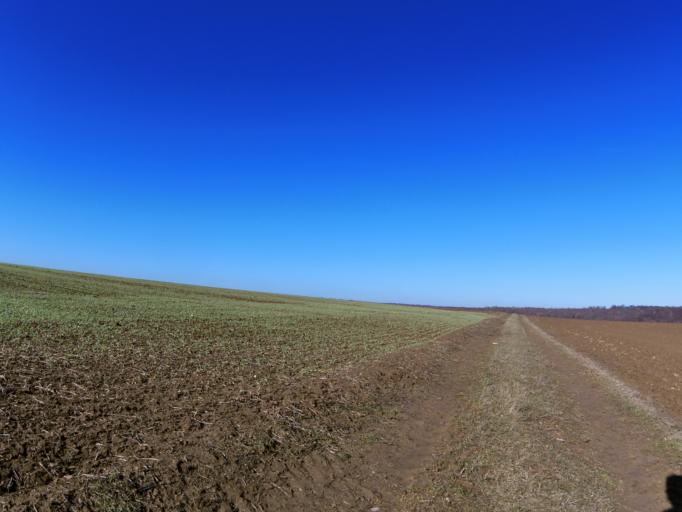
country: DE
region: Bavaria
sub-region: Regierungsbezirk Unterfranken
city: Estenfeld
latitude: 49.8455
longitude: 9.9911
